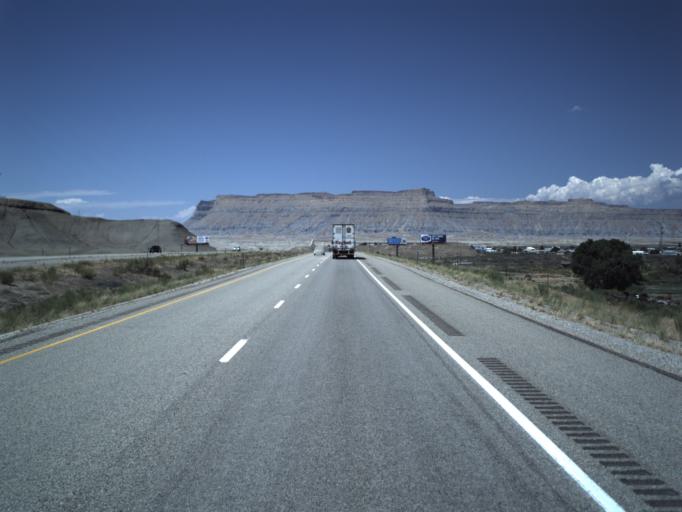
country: US
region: Utah
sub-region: Carbon County
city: East Carbon City
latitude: 38.9801
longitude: -110.1614
